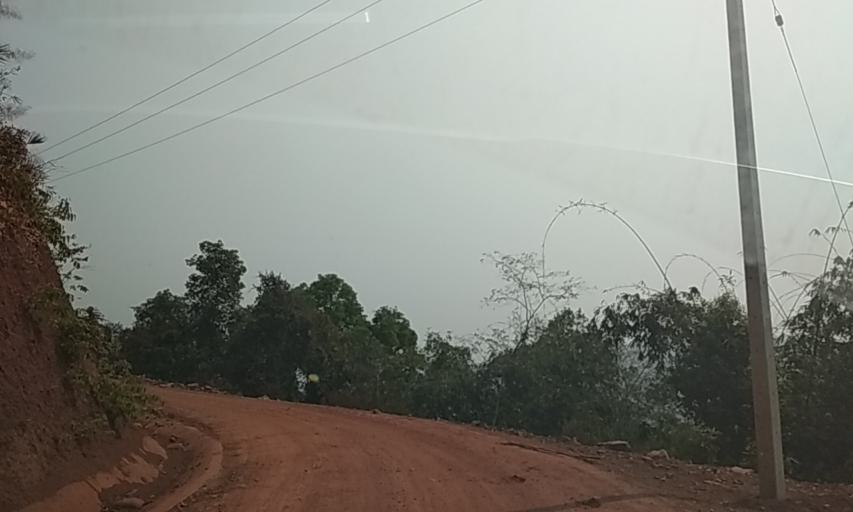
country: VN
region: Huyen Dien Bien
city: Dien Bien Phu
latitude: 21.4525
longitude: 102.7673
